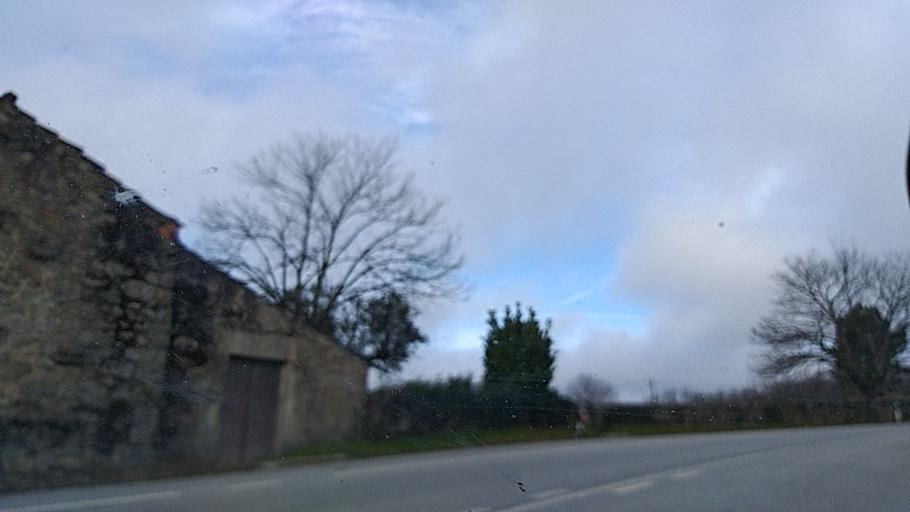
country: PT
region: Guarda
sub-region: Aguiar da Beira
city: Aguiar da Beira
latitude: 40.7264
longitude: -7.4962
